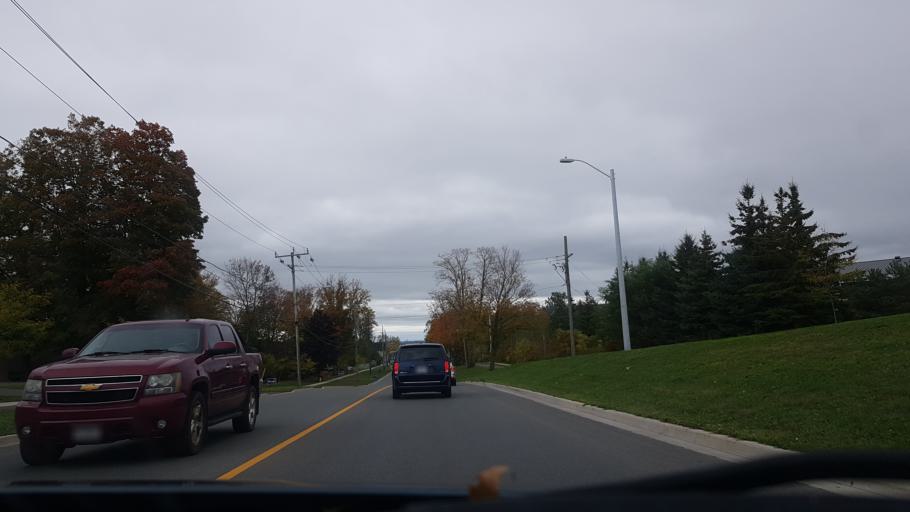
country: CA
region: Ontario
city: Peterborough
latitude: 44.2698
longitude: -78.3694
